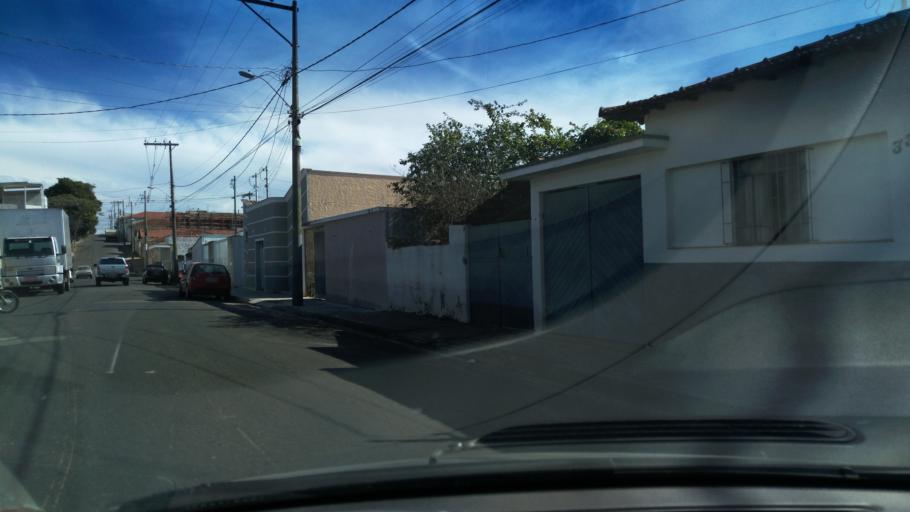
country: BR
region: Minas Gerais
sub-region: Andradas
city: Andradas
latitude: -22.0736
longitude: -46.5714
